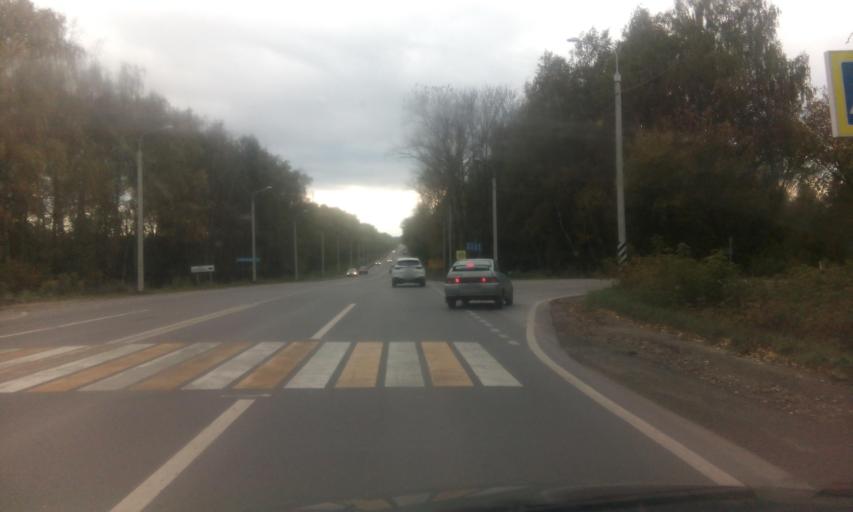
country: RU
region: Tula
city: Kamenetskiy
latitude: 54.0013
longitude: 38.2348
